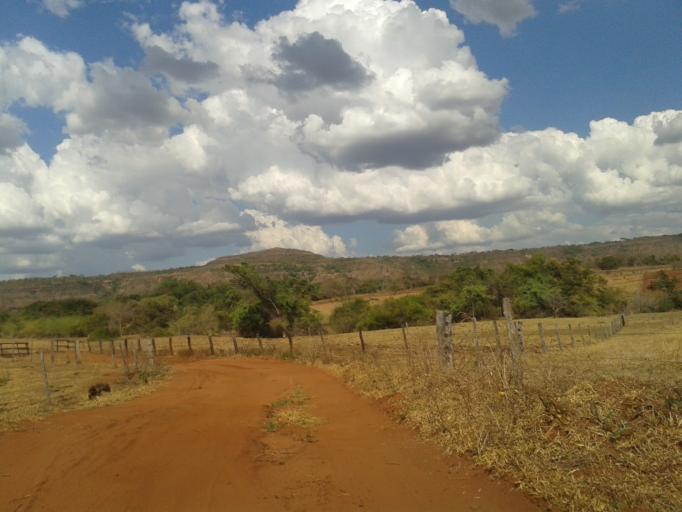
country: BR
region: Minas Gerais
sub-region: Santa Vitoria
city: Santa Vitoria
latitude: -19.2089
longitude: -49.9663
